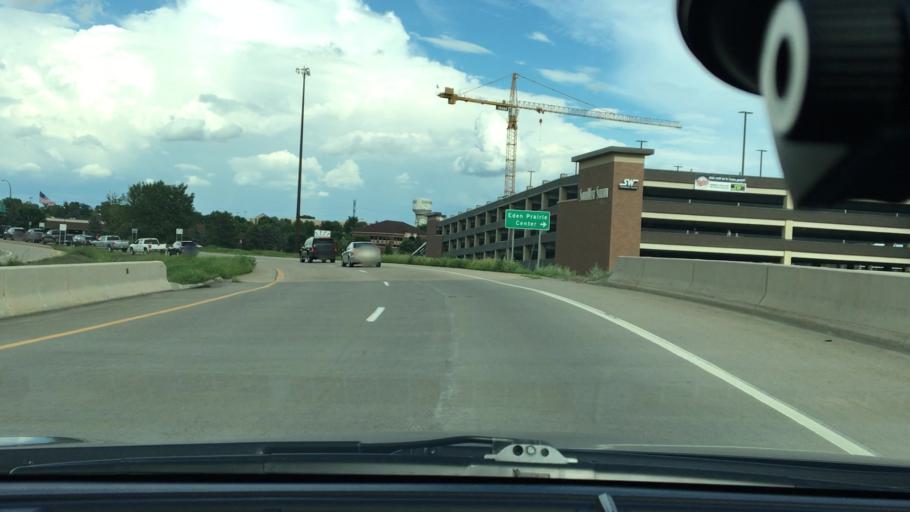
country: US
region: Minnesota
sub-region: Hennepin County
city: Eden Prairie
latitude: 44.8605
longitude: -93.4444
